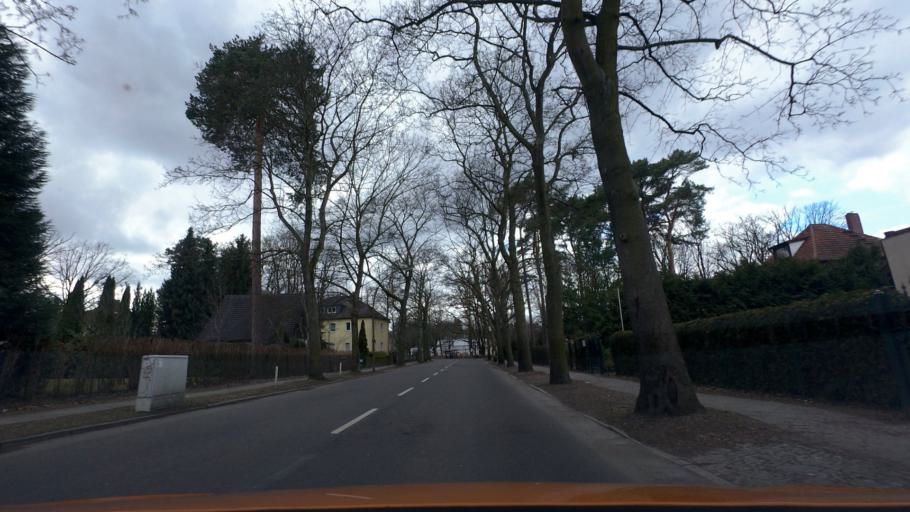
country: DE
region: Berlin
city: Konradshohe
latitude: 52.5853
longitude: 13.2292
